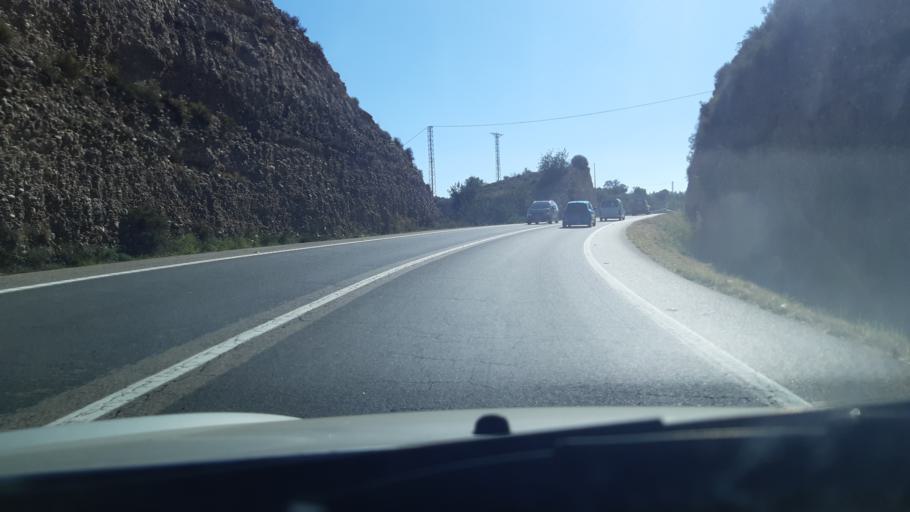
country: ES
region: Catalonia
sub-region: Provincia de Tarragona
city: Tivenys
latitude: 40.8809
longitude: 0.4976
